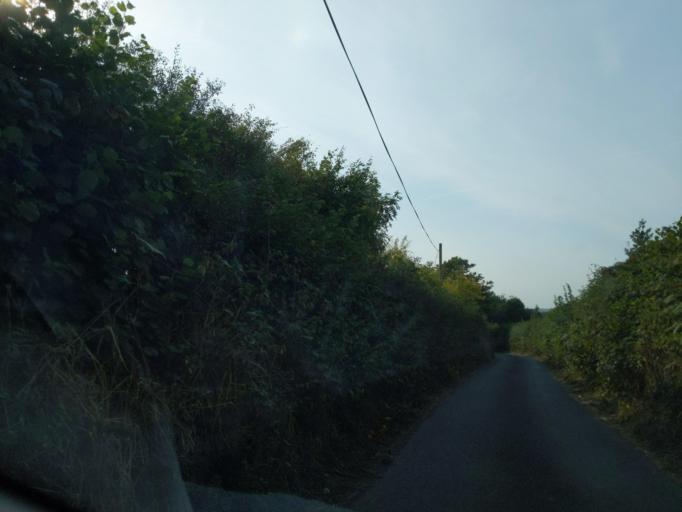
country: GB
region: England
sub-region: Devon
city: Winkleigh
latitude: 50.9660
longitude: -3.9904
